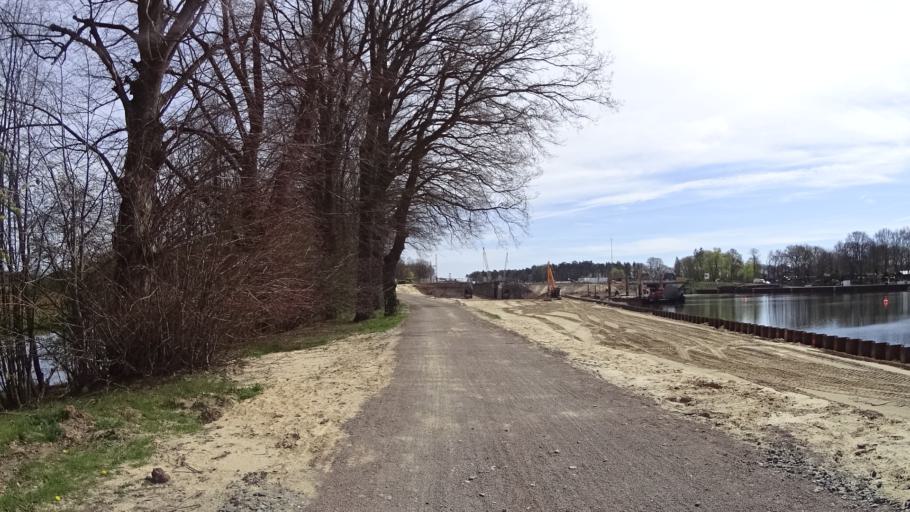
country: DE
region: Lower Saxony
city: Lingen
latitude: 52.4591
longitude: 7.3264
